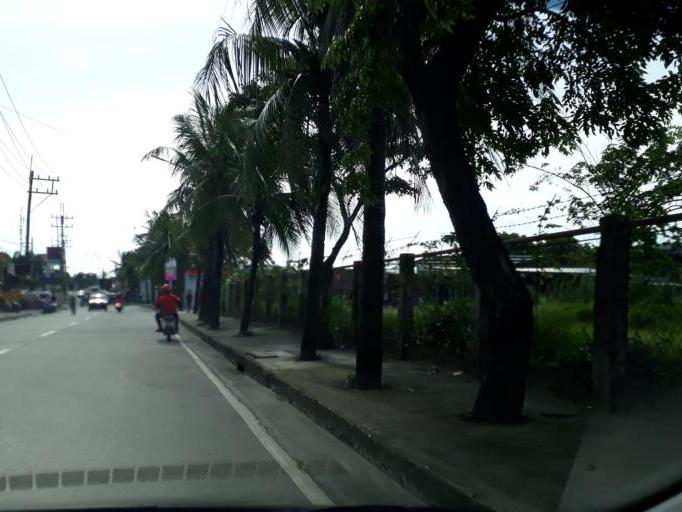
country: PH
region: Metro Manila
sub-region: Caloocan City
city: Niugan
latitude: 14.6709
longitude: 120.9552
